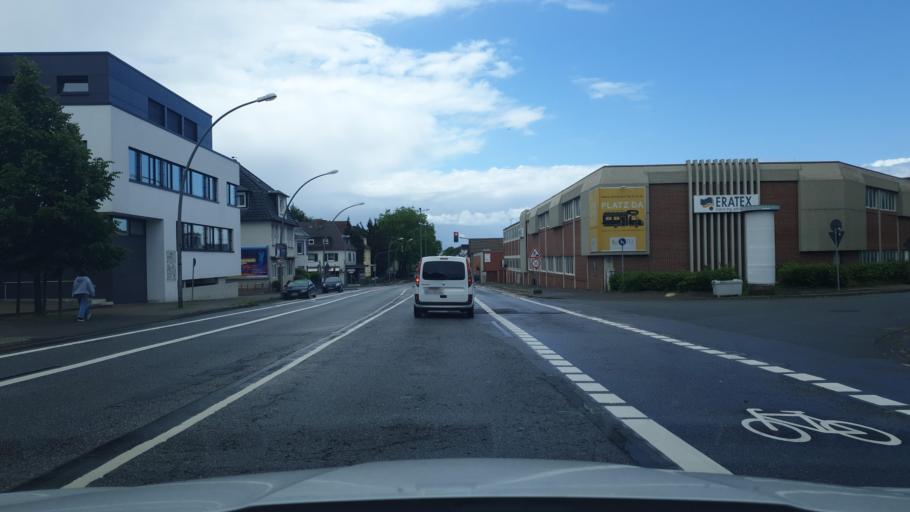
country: DE
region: North Rhine-Westphalia
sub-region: Regierungsbezirk Detmold
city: Herford
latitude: 52.1246
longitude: 8.6832
